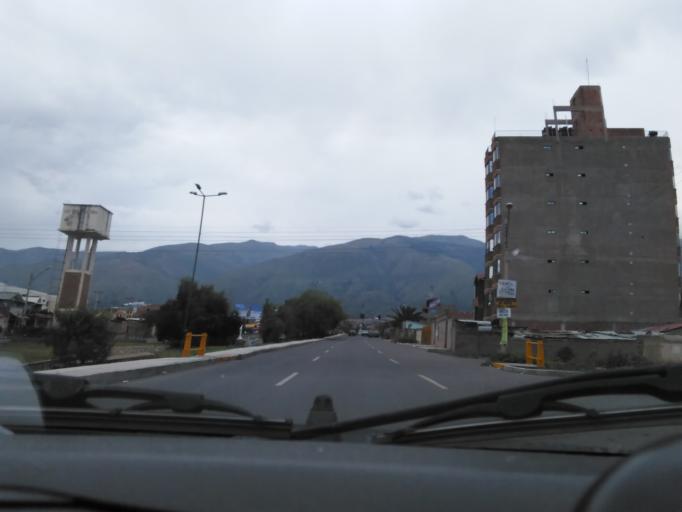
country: BO
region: Cochabamba
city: Cochabamba
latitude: -17.3658
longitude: -66.1788
